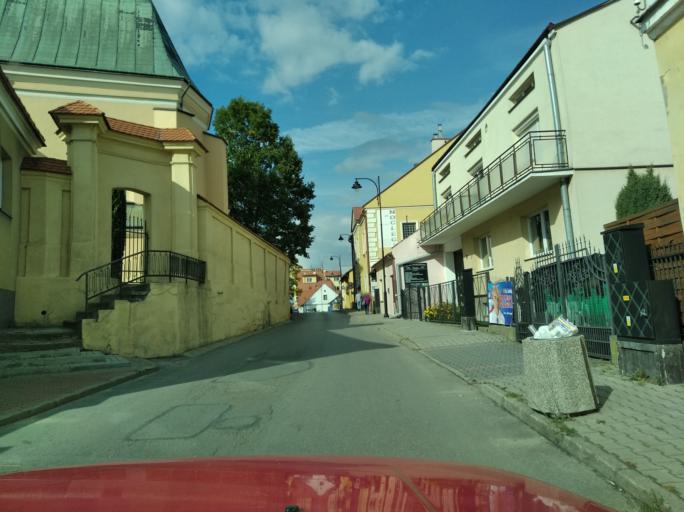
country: PL
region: Subcarpathian Voivodeship
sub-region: Powiat rzeszowski
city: Tyczyn
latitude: 49.9617
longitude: 22.0343
